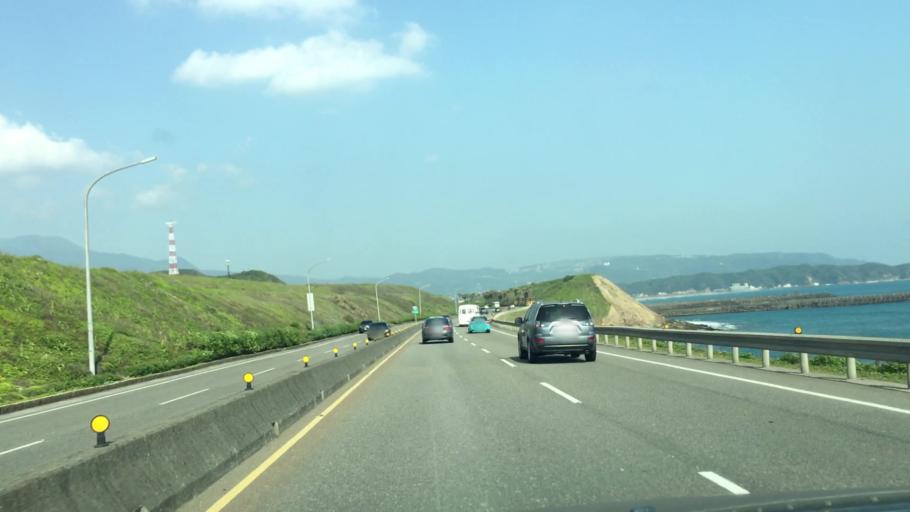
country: TW
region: Taiwan
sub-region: Keelung
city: Keelung
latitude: 25.2031
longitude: 121.6689
